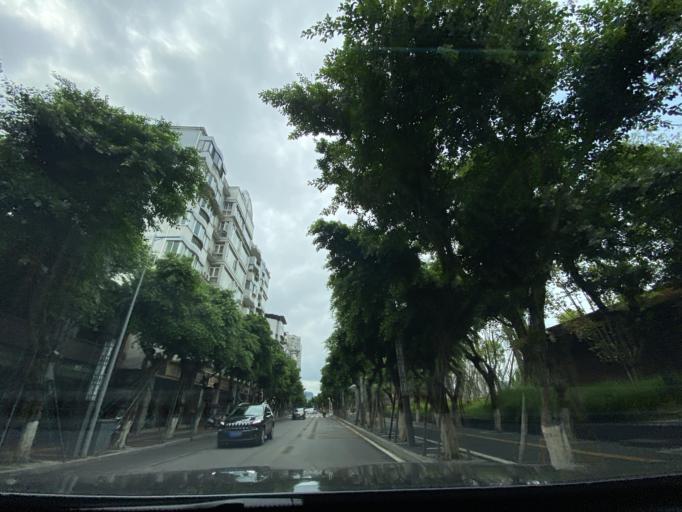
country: CN
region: Sichuan
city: Jiancheng
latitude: 30.3944
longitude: 104.5535
